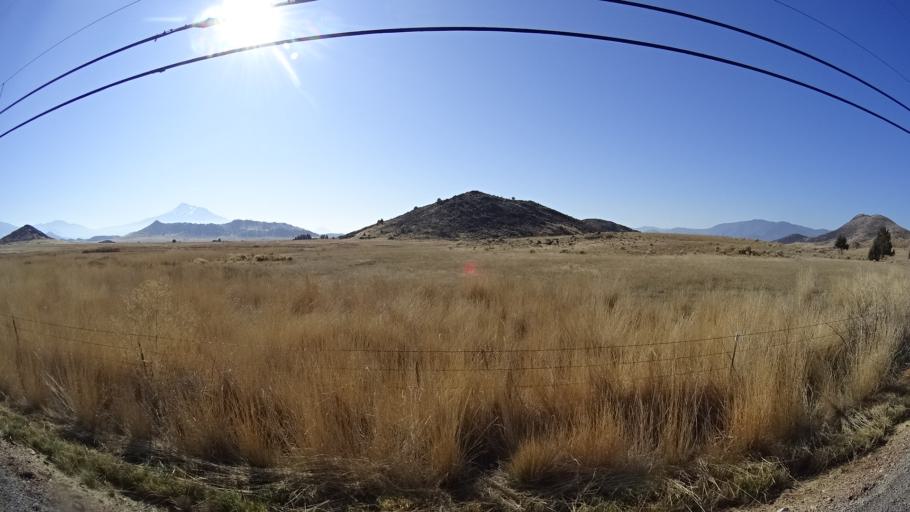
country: US
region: California
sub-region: Siskiyou County
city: Montague
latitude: 41.7269
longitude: -122.4899
